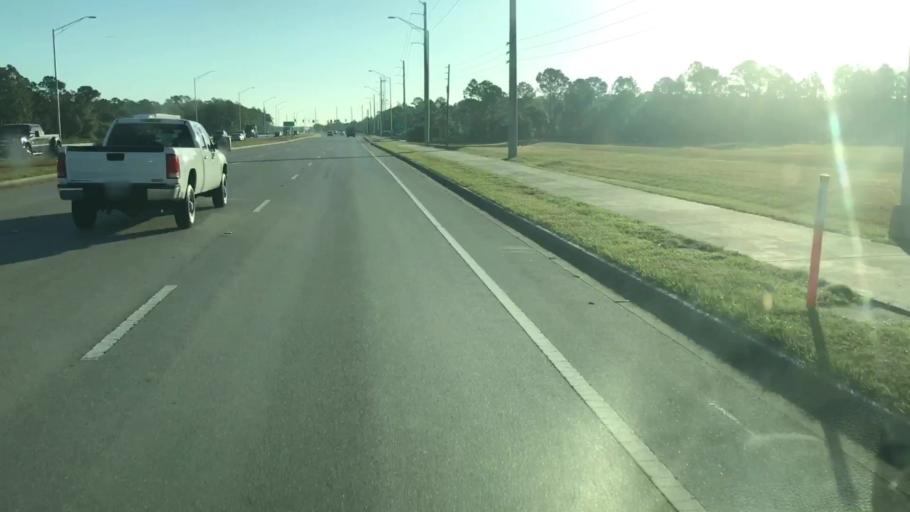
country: US
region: Florida
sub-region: Collier County
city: Orangetree
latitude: 26.2761
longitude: -81.6112
